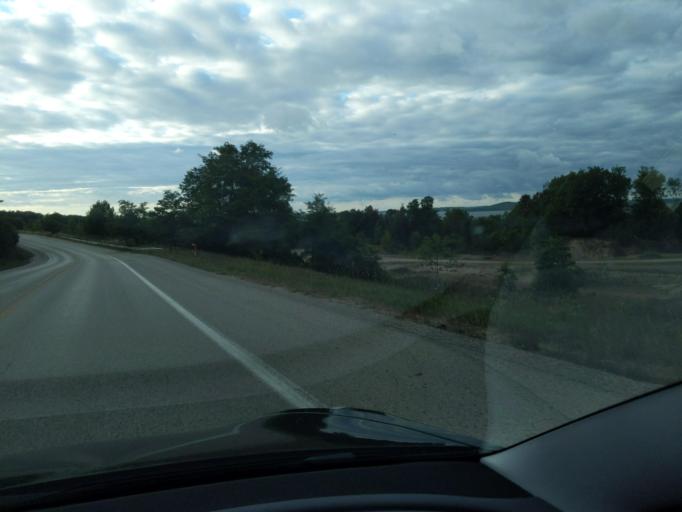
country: US
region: Michigan
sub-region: Kalkaska County
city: Rapid City
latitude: 44.7814
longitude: -85.2828
